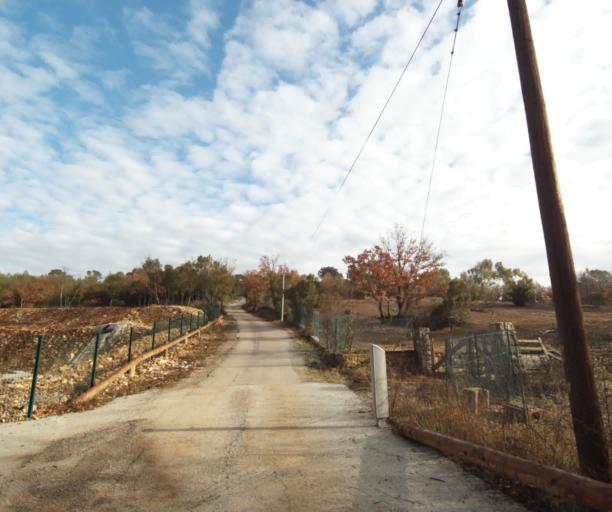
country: FR
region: Provence-Alpes-Cote d'Azur
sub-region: Departement du Var
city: Trans-en-Provence
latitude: 43.4943
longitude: 6.4748
